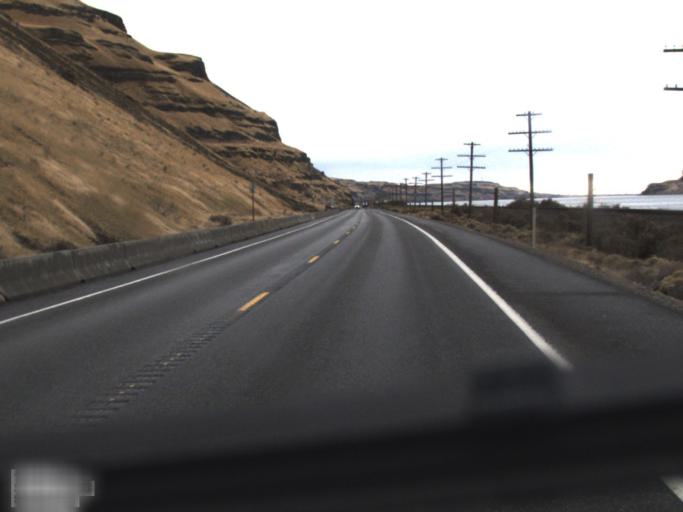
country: US
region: Washington
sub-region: Benton County
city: Finley
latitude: 46.0027
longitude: -118.9732
